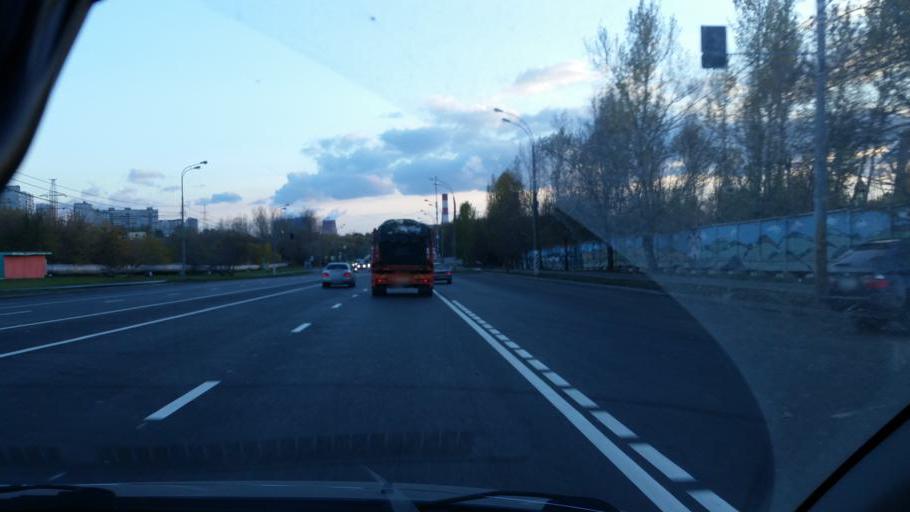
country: RU
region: Moskovskaya
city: Biryulevo Zapadnoye
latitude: 55.5987
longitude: 37.6364
